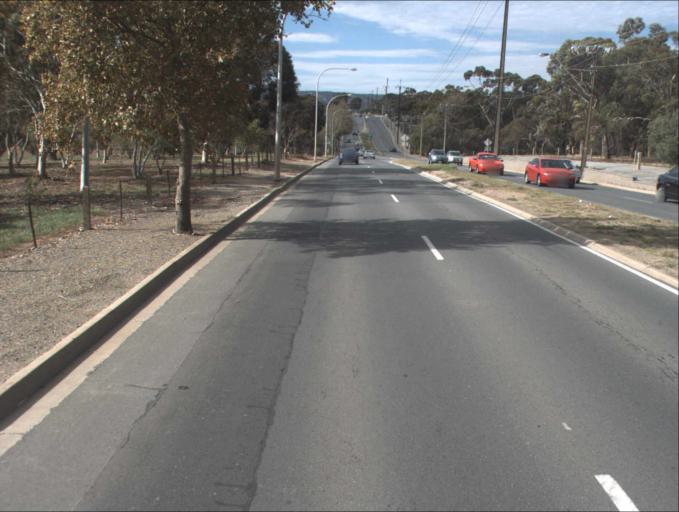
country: AU
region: South Australia
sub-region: Port Adelaide Enfield
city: Gilles Plains
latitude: -34.8463
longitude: 138.6436
